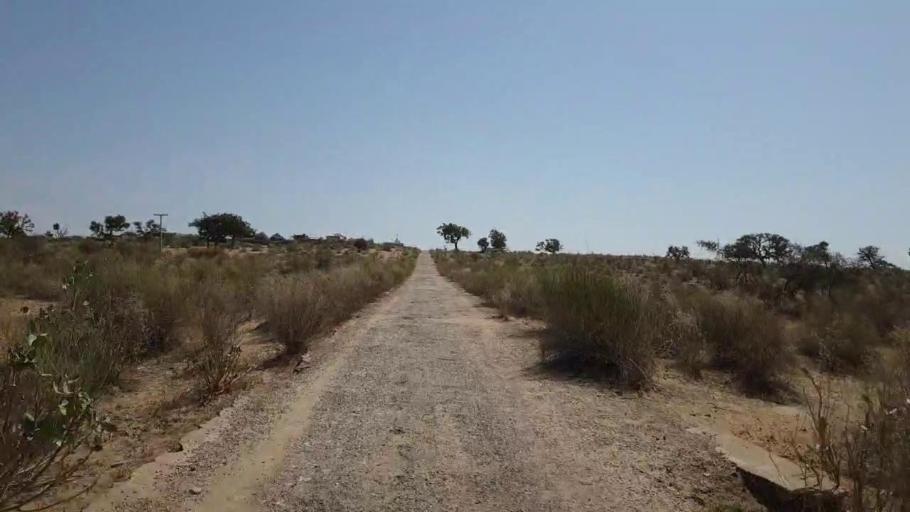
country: PK
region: Sindh
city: Nabisar
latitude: 25.1067
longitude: 69.9023
